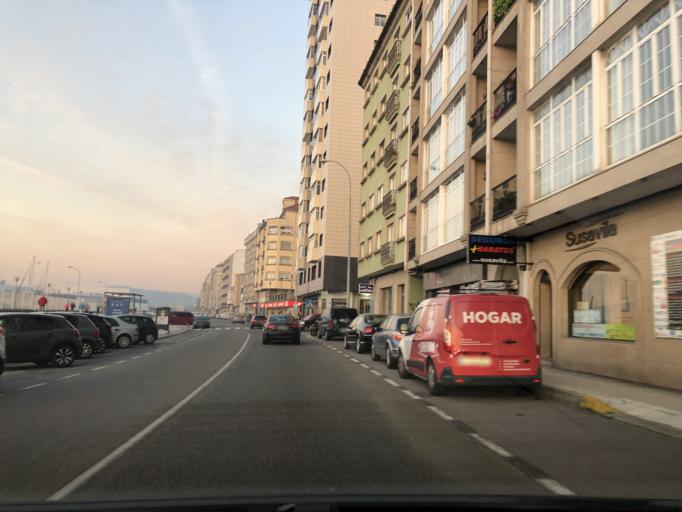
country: ES
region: Galicia
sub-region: Provincia de Pontevedra
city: Marin
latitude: 42.3946
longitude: -8.6939
